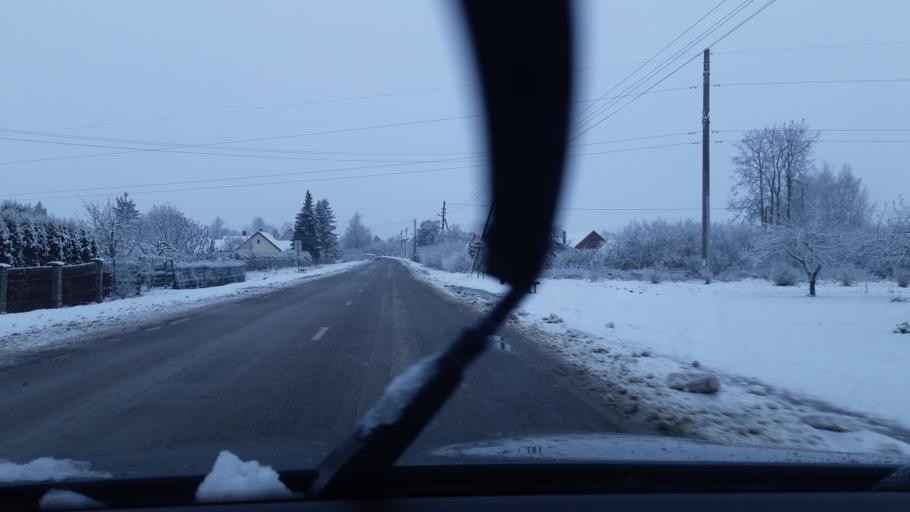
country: LT
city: Kaisiadorys
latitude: 54.8439
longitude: 24.3427
